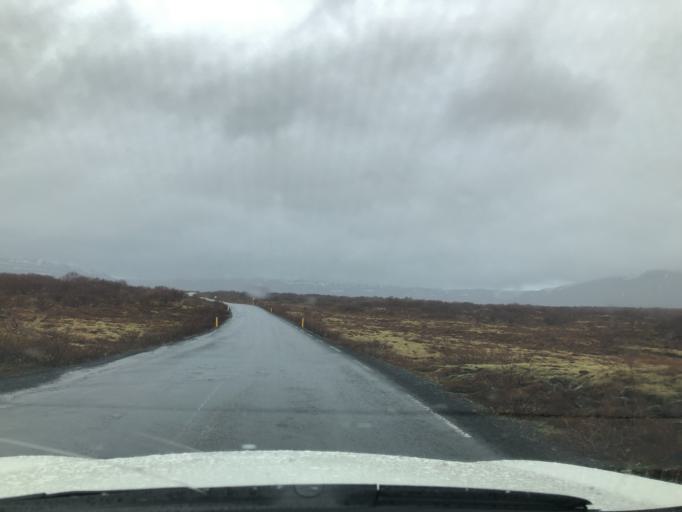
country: IS
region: South
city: Hveragerdi
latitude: 64.2636
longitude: -21.0541
